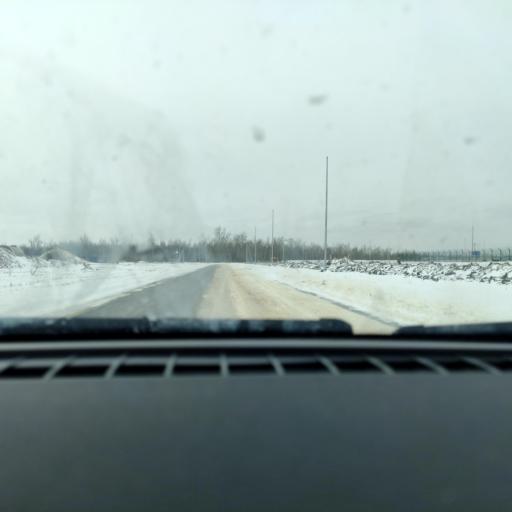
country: RU
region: Voronezj
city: Maslovka
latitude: 51.5403
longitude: 39.2781
